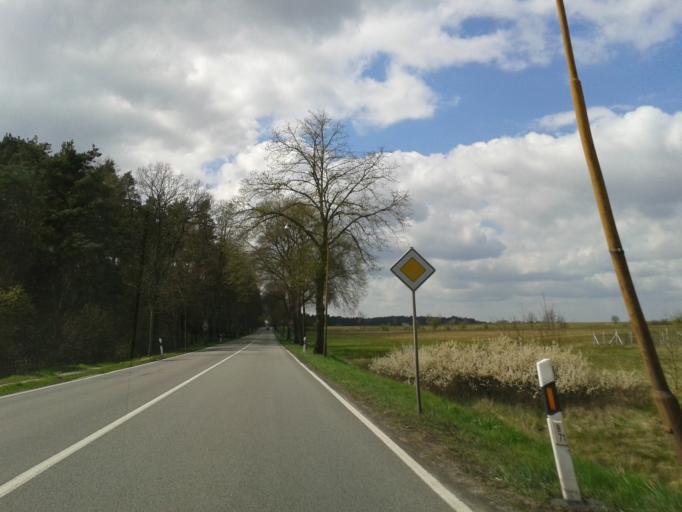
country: DE
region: Lower Saxony
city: Bergen an der Dumme
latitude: 52.8802
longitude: 11.0340
